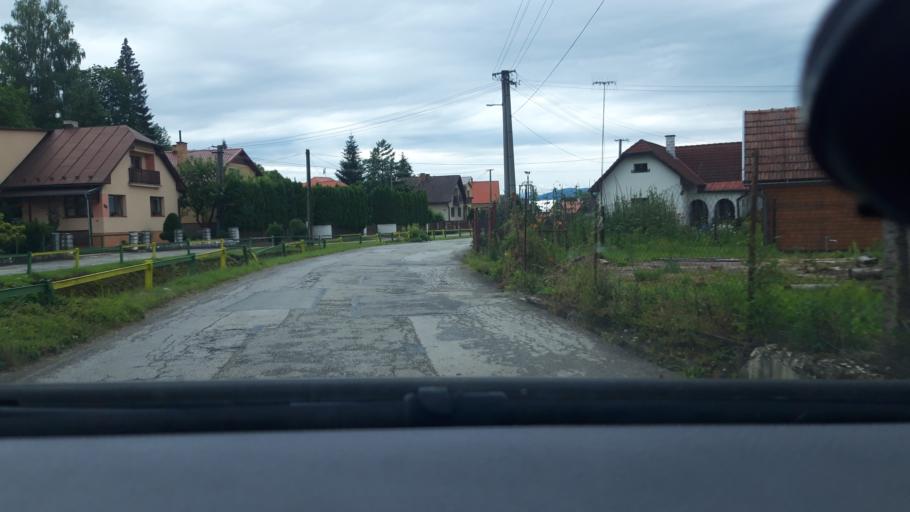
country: SK
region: Zilinsky
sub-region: Okres Martin
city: Martin
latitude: 49.0013
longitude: 18.9863
